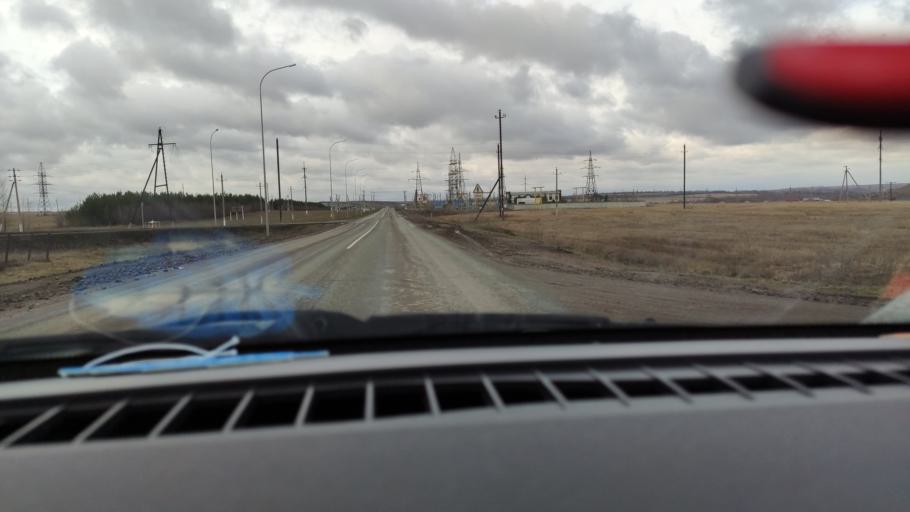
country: RU
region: Tatarstan
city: Cheremshan
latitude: 54.9227
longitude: 51.6753
